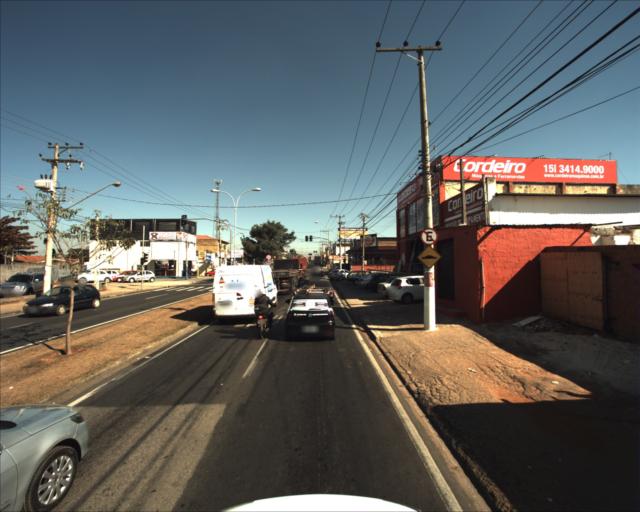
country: BR
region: Sao Paulo
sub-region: Sorocaba
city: Sorocaba
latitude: -23.4223
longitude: -47.4124
